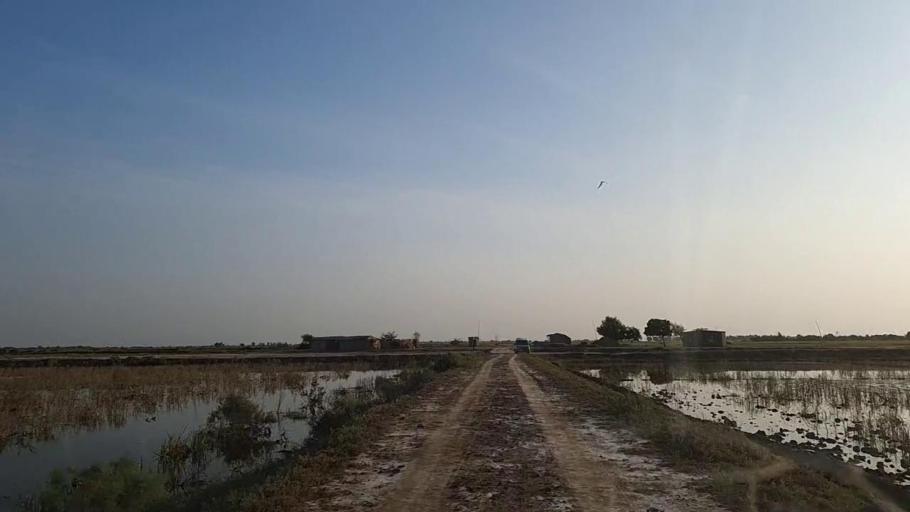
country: PK
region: Sindh
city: Mirpur Batoro
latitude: 24.6063
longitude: 68.1025
